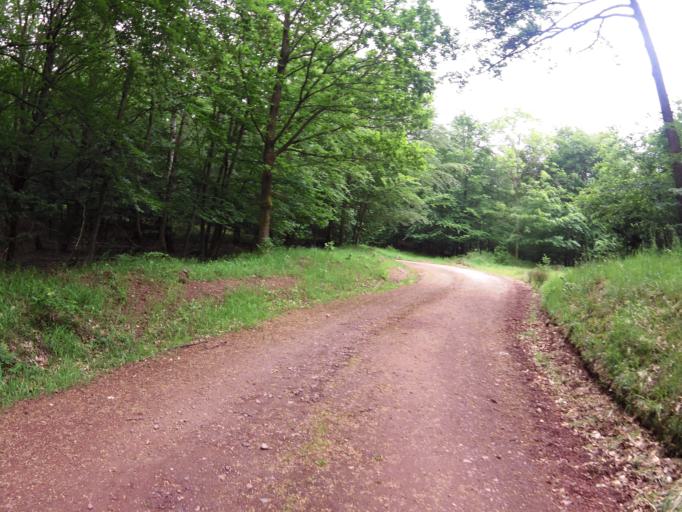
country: DE
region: Thuringia
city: Eisenach
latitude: 50.9416
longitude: 10.3234
